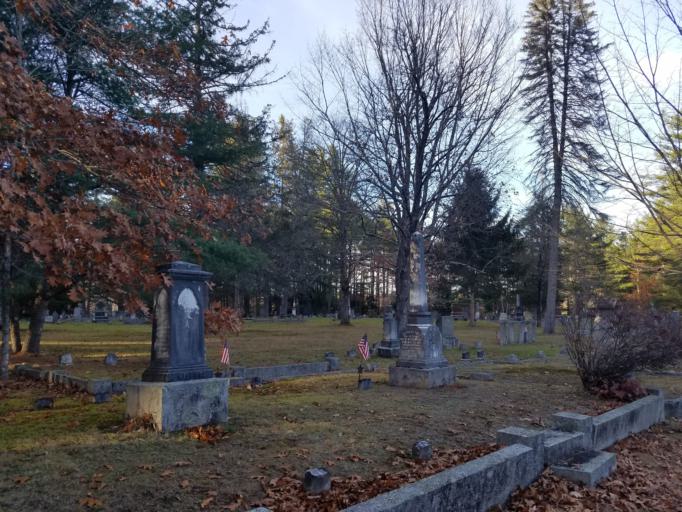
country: US
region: New Hampshire
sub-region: Merrimack County
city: Henniker
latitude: 43.1803
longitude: -71.8139
